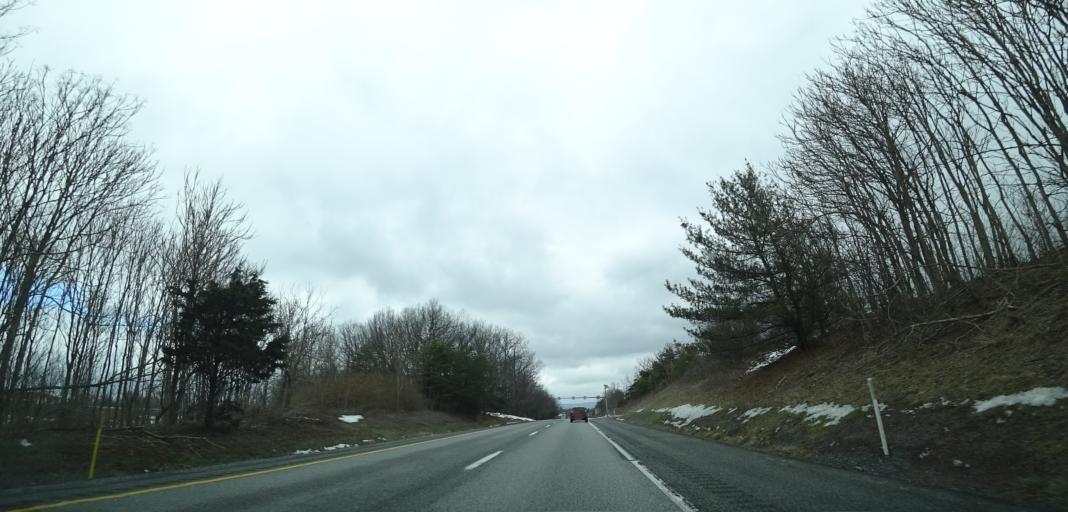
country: US
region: Pennsylvania
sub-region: Bedford County
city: Earlston
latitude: 39.9942
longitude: -78.2403
